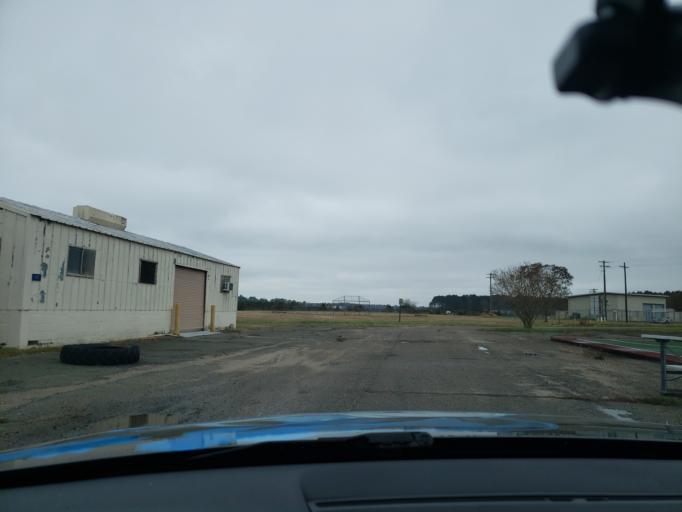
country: US
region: Virginia
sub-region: City of Chesapeake
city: Chesapeake
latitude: 36.7056
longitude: -76.1275
